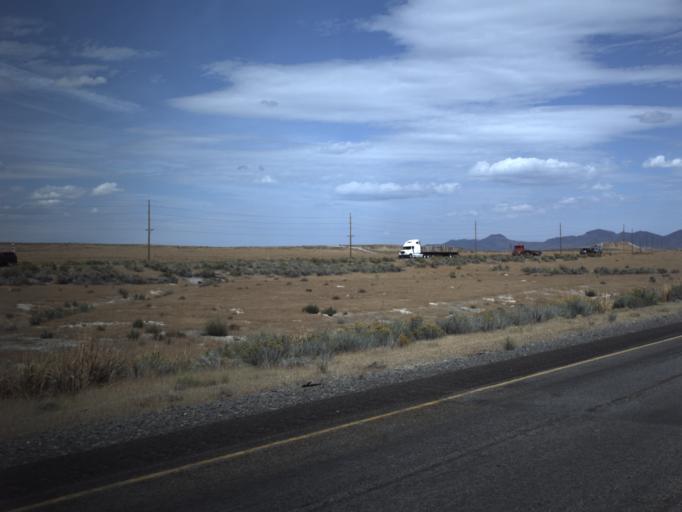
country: US
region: Utah
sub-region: Tooele County
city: Grantsville
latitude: 40.7637
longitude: -112.9967
